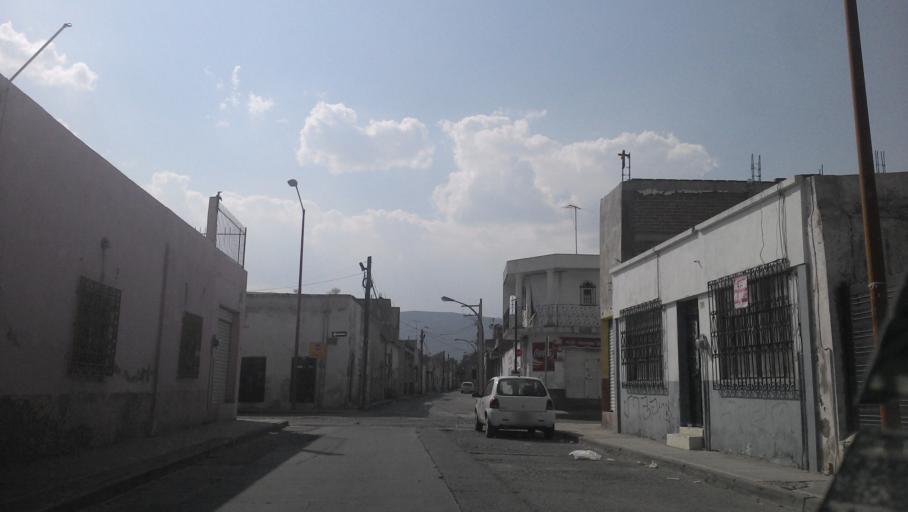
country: MX
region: Guanajuato
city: San Francisco del Rincon
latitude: 21.0213
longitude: -101.8599
